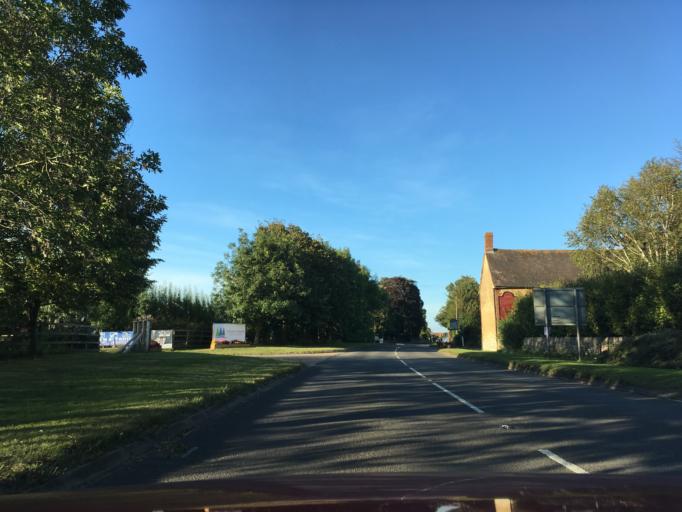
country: GB
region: England
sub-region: Worcestershire
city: Bredon
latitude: 52.0156
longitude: -2.1303
